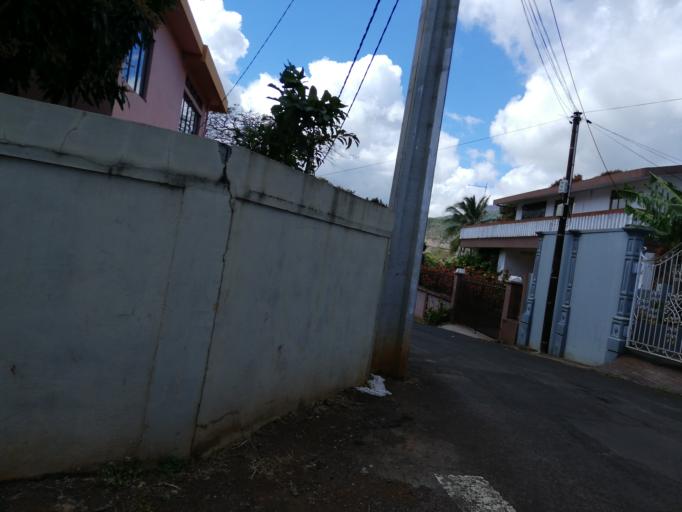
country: MU
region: Moka
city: Pailles
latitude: -20.2021
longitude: 57.4719
